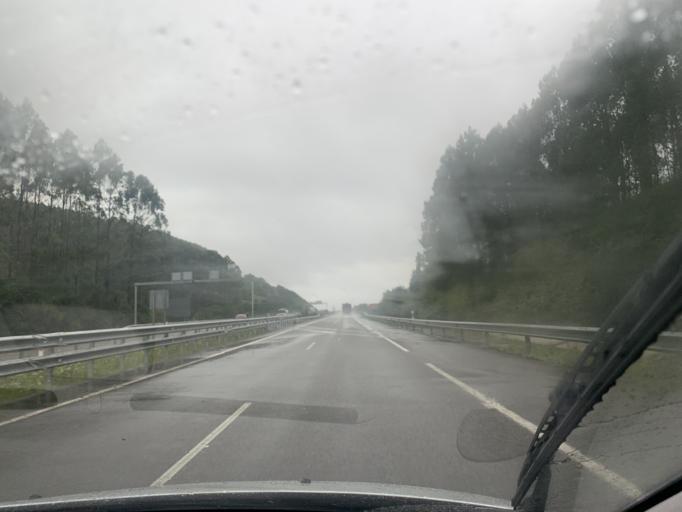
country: ES
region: Galicia
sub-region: Provincia de Lugo
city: Mondonedo
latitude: 43.3774
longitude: -7.4347
